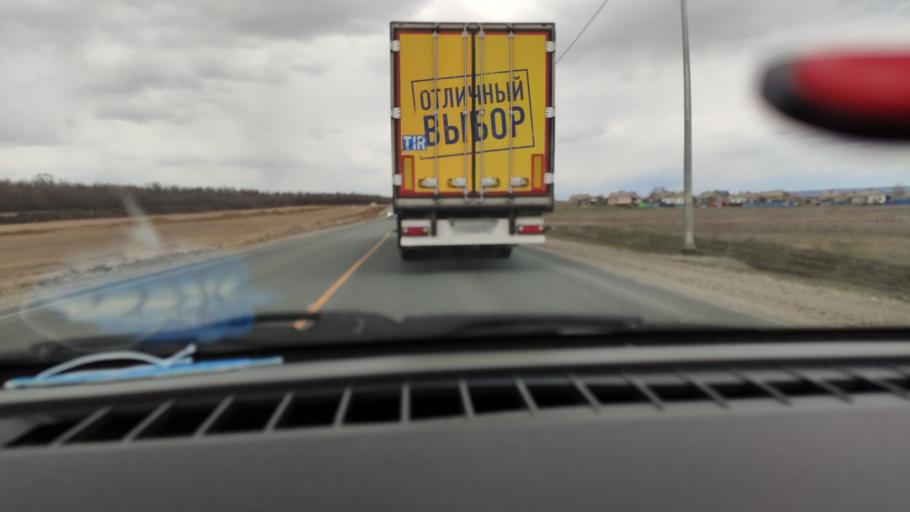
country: RU
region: Saratov
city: Sennoy
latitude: 52.1588
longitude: 47.0664
